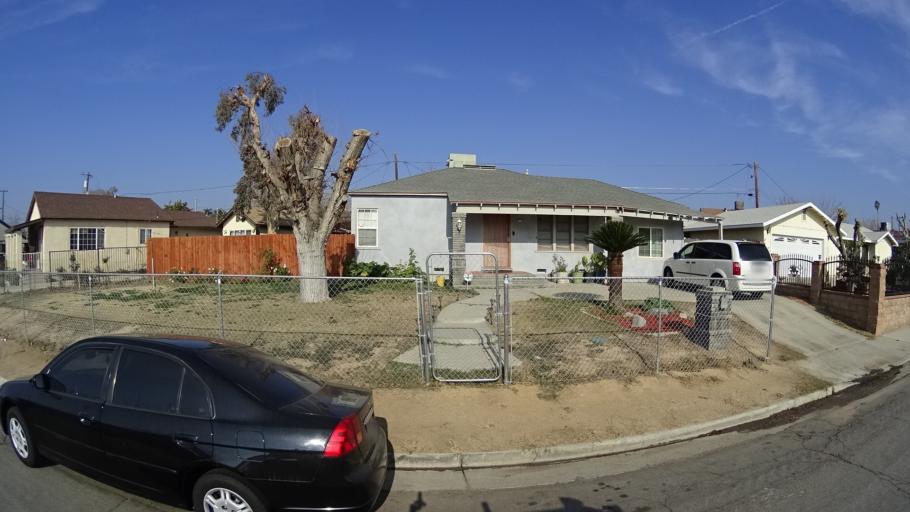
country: US
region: California
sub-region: Kern County
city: Bakersfield
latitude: 35.3867
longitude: -118.9749
